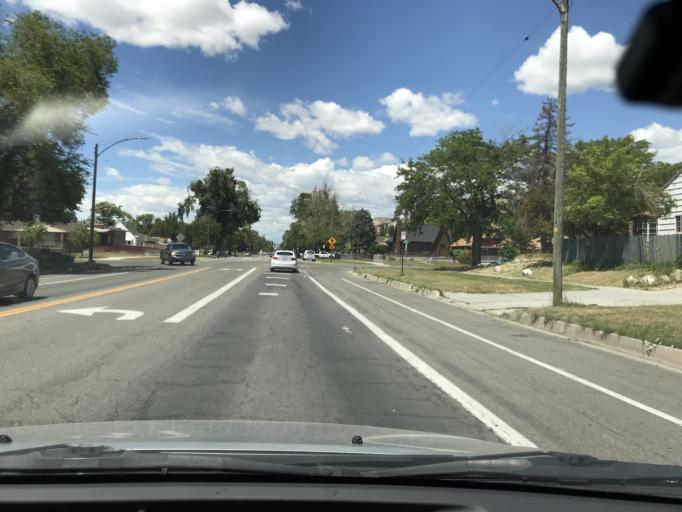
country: US
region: Utah
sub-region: Salt Lake County
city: Salt Lake City
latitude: 40.7796
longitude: -111.9168
